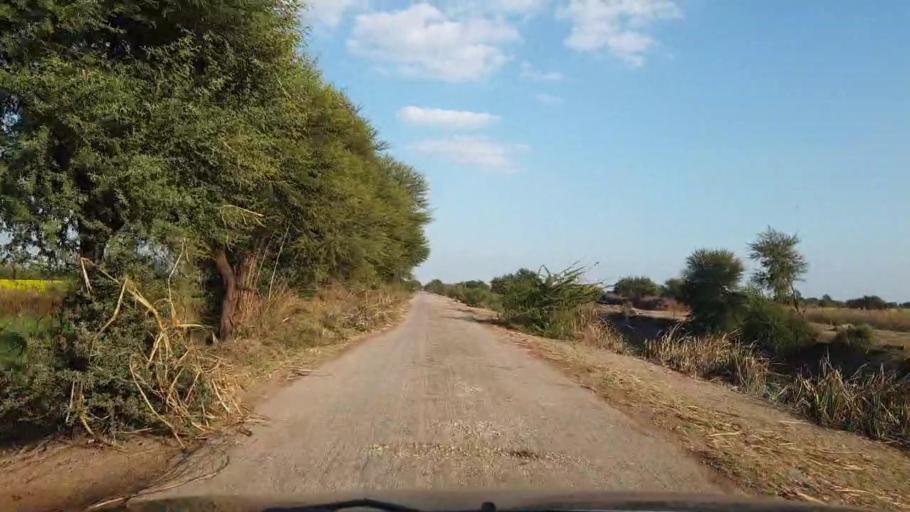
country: PK
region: Sindh
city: Sinjhoro
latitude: 25.9956
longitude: 68.7409
